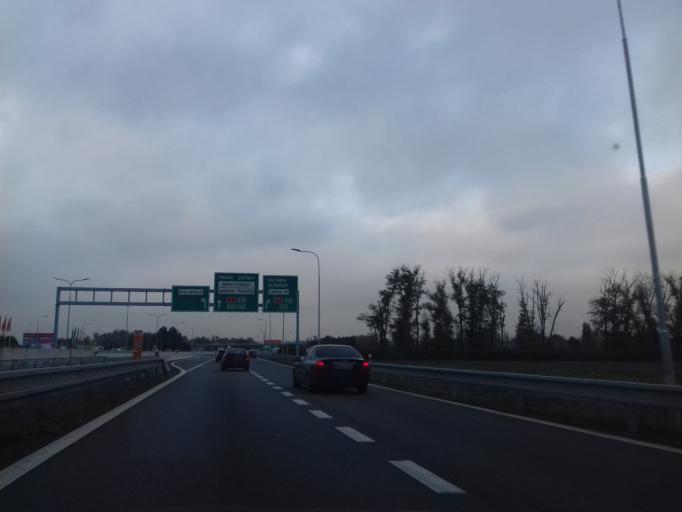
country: CZ
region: South Moravian
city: Modrice
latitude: 49.1541
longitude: 16.6304
